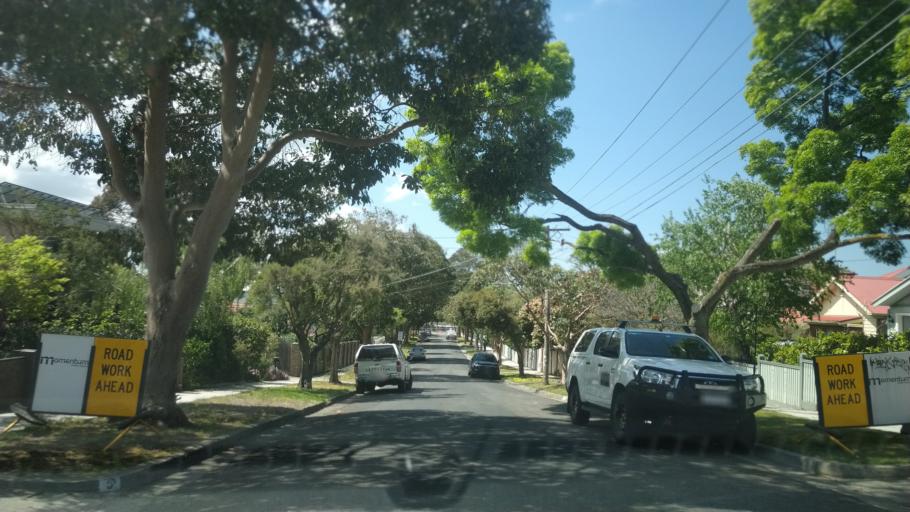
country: AU
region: Victoria
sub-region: Bayside
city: Cheltenham
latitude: -37.9626
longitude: 145.0496
